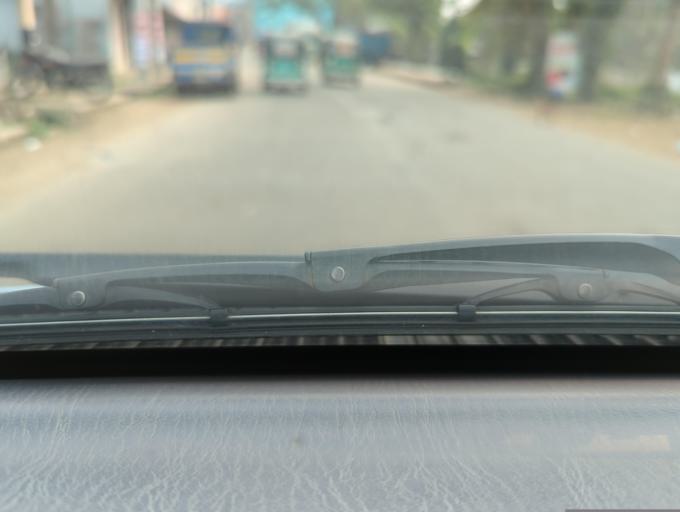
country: BD
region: Sylhet
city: Maulavi Bazar
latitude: 24.4896
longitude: 91.7478
